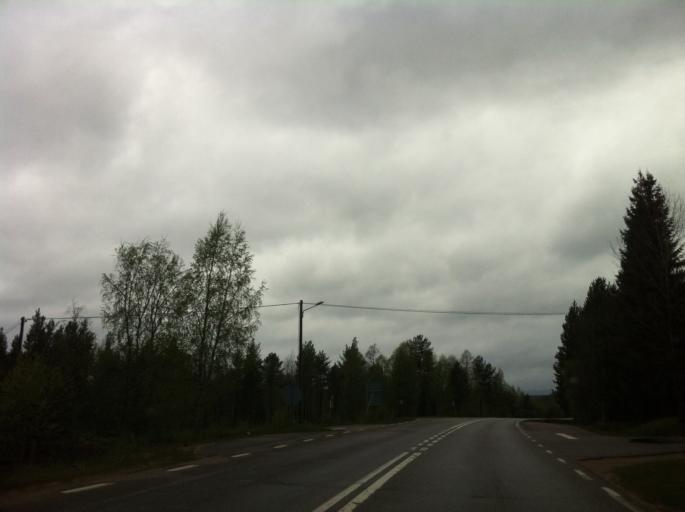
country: SE
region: Jaemtland
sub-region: Harjedalens Kommun
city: Sveg
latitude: 62.1252
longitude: 14.0723
